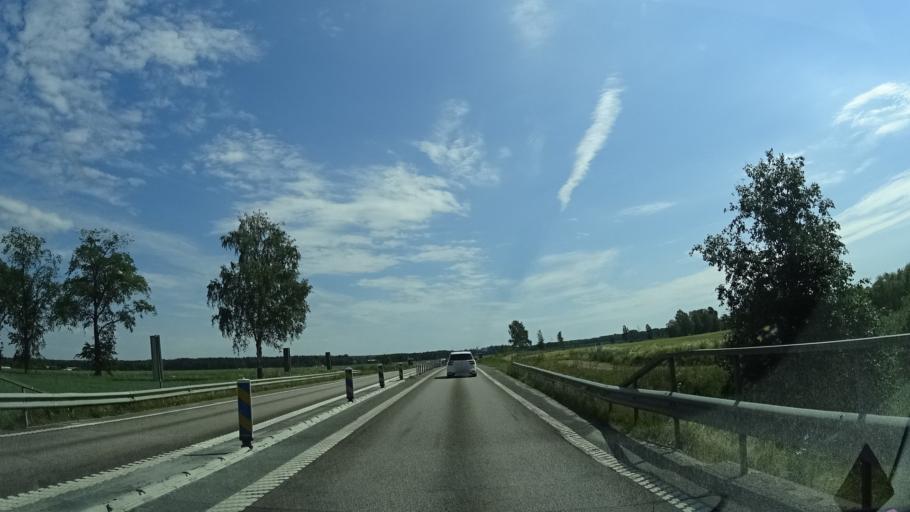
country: SE
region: Vaermland
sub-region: Kristinehamns Kommun
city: Kristinehamn
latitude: 59.3751
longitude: 13.9720
